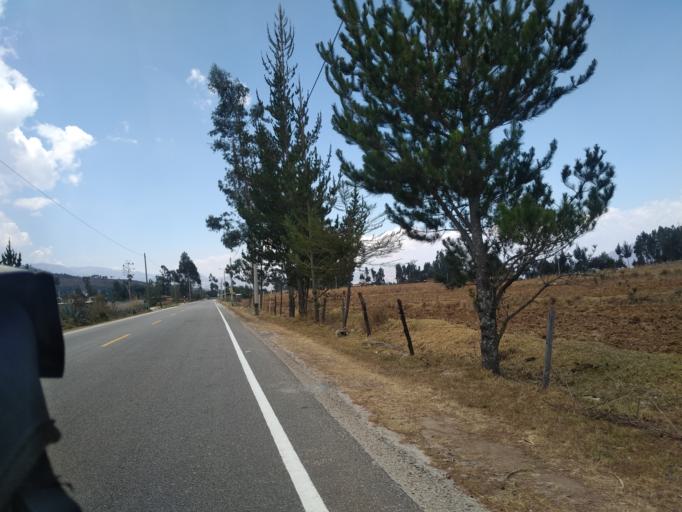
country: PE
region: Cajamarca
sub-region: San Marcos
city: San Marcos
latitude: -7.2813
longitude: -78.2296
